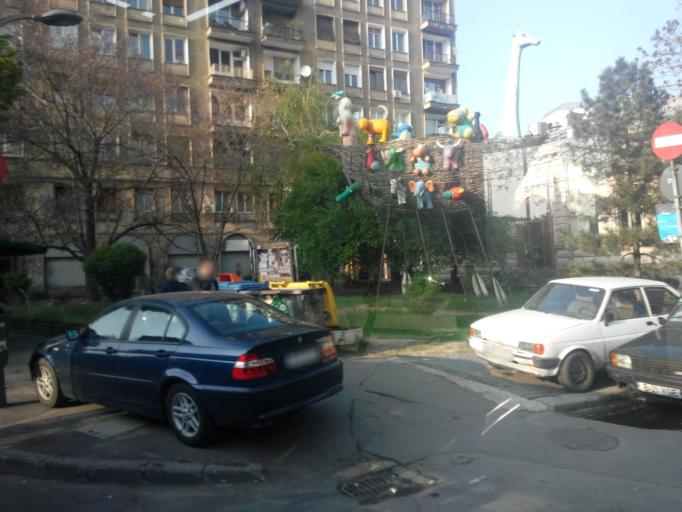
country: RO
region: Bucuresti
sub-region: Municipiul Bucuresti
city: Bucharest
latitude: 44.4425
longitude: 26.0987
